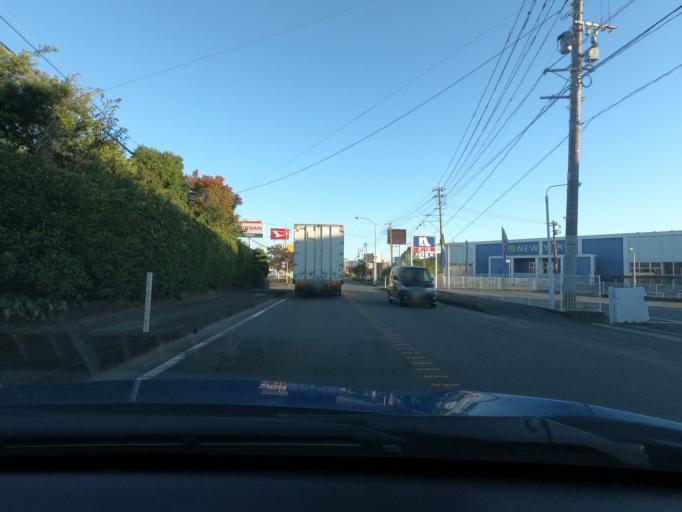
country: JP
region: Kagoshima
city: Satsumasendai
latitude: 31.8382
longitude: 130.2845
